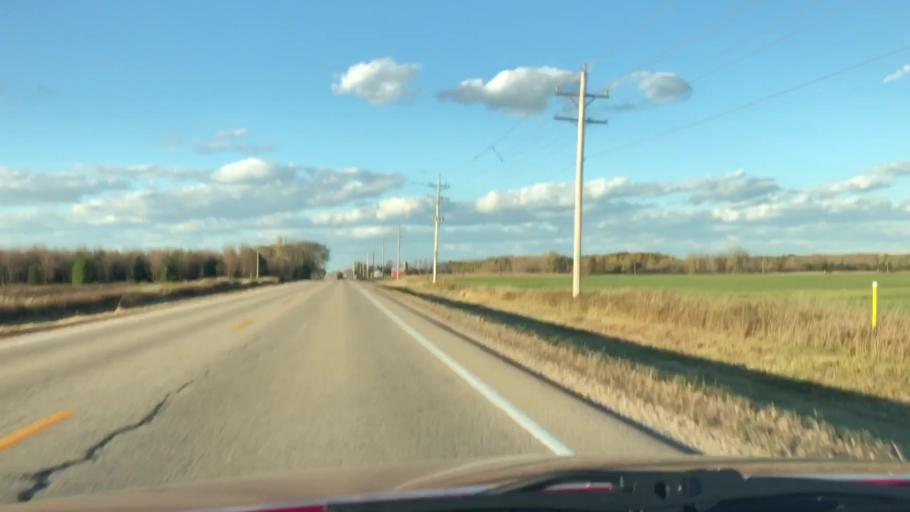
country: US
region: Wisconsin
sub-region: Outagamie County
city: Seymour
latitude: 44.4682
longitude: -88.2911
